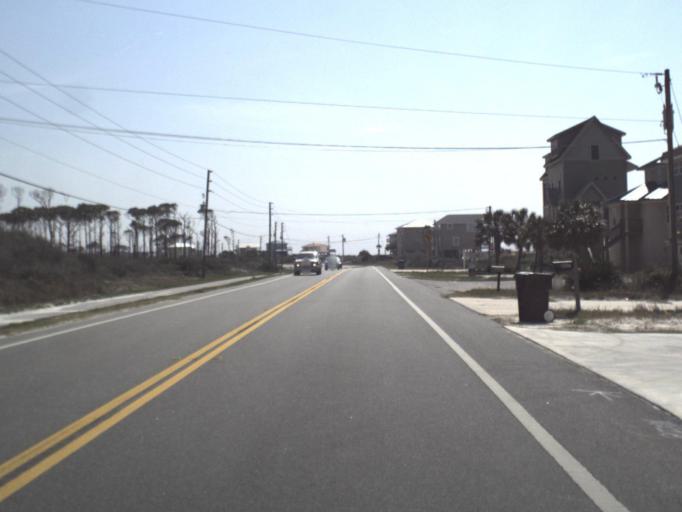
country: US
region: Florida
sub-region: Gulf County
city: Port Saint Joe
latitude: 29.6903
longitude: -85.3725
